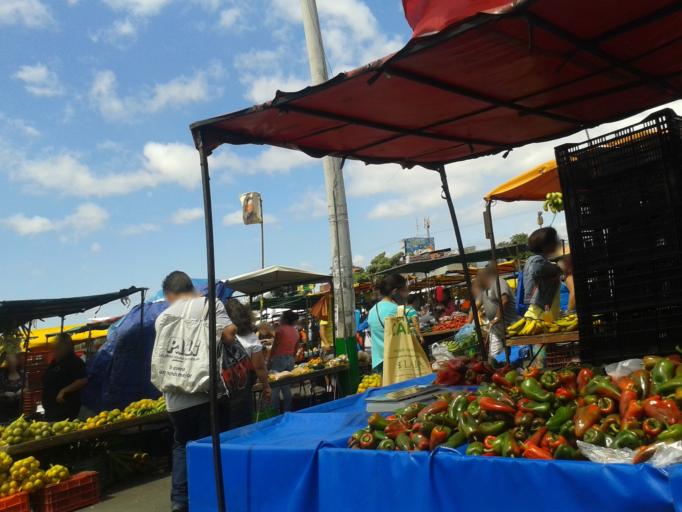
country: CR
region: San Jose
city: San Pedro
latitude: 9.9184
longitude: -84.0545
